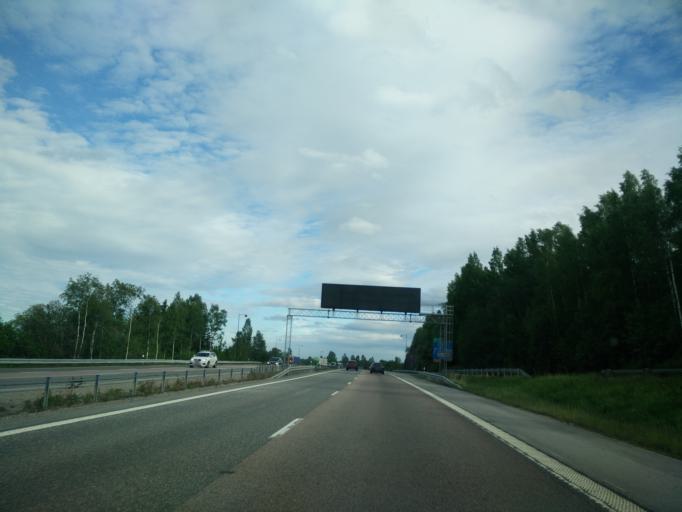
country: SE
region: Vaesternorrland
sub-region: Sundsvalls Kommun
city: Sundsbruk
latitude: 62.4599
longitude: 17.3409
